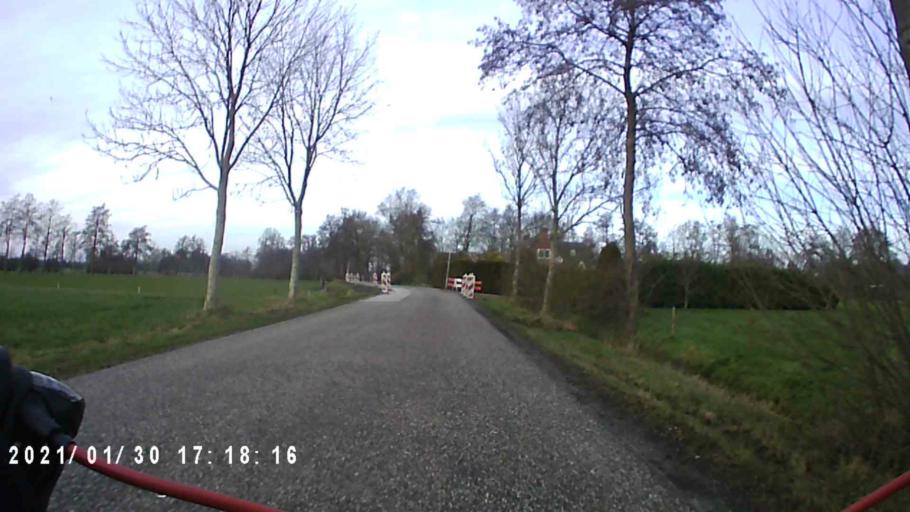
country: NL
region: Groningen
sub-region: Gemeente Leek
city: Leek
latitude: 53.1851
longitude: 6.3576
